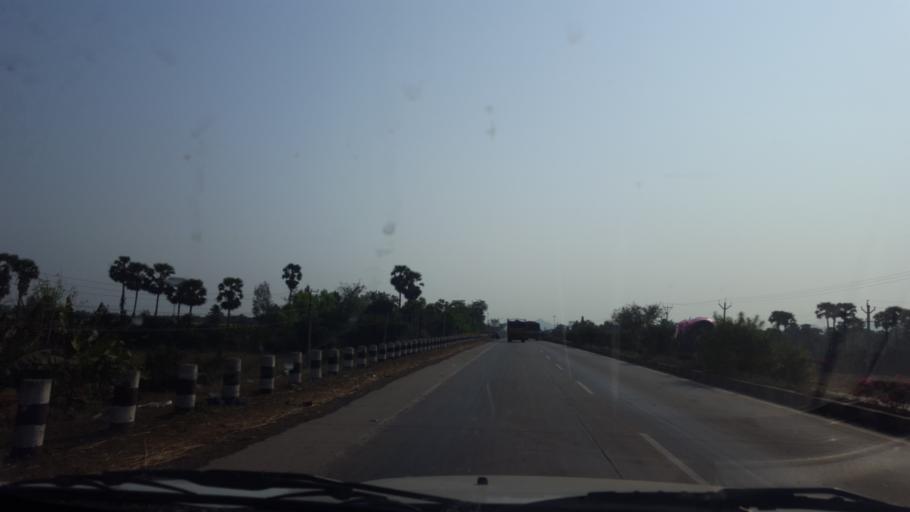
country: IN
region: Andhra Pradesh
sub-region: Vishakhapatnam
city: Elamanchili
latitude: 17.5921
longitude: 82.8710
